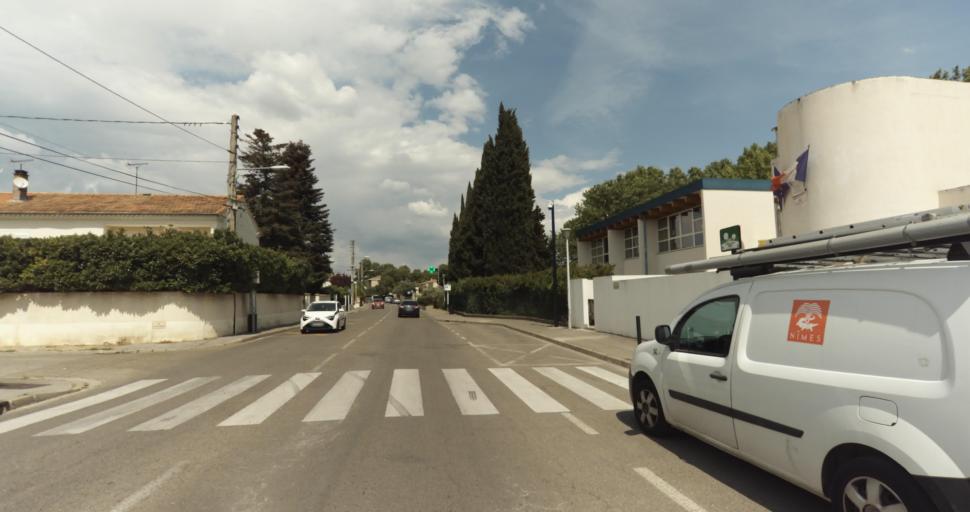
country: FR
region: Languedoc-Roussillon
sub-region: Departement du Gard
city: Nimes
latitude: 43.8347
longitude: 4.3837
